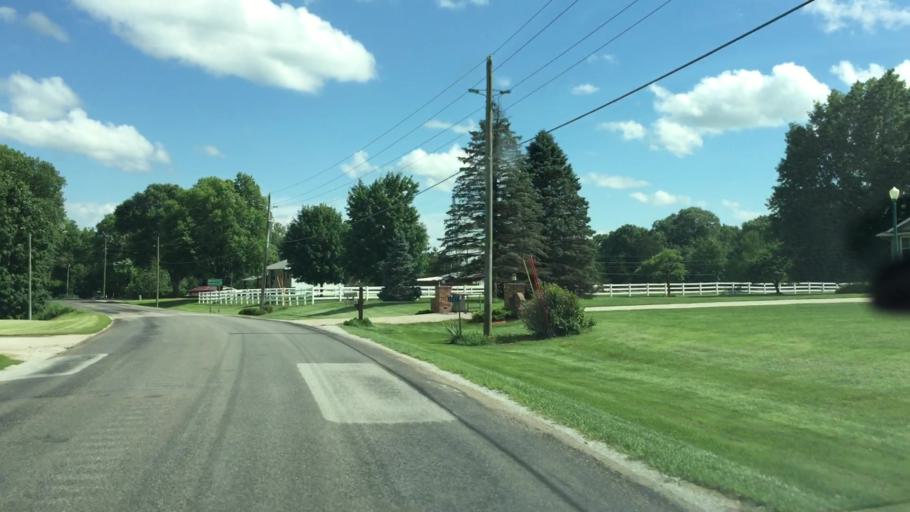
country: US
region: Iowa
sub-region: Linn County
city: Ely
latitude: 41.8229
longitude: -91.6246
